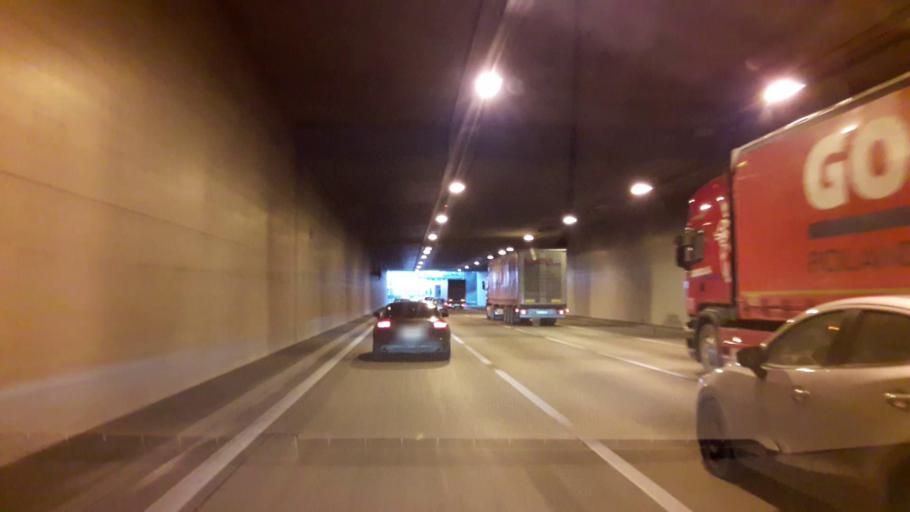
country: AT
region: Vienna
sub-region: Wien Stadt
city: Vienna
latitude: 48.1673
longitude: 16.3891
